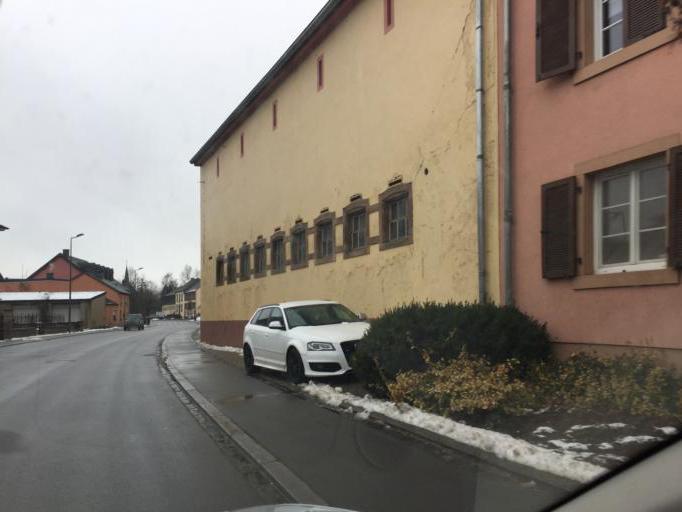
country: LU
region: Diekirch
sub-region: Canton de Diekirch
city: Mertzig
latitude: 49.8343
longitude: 6.0084
